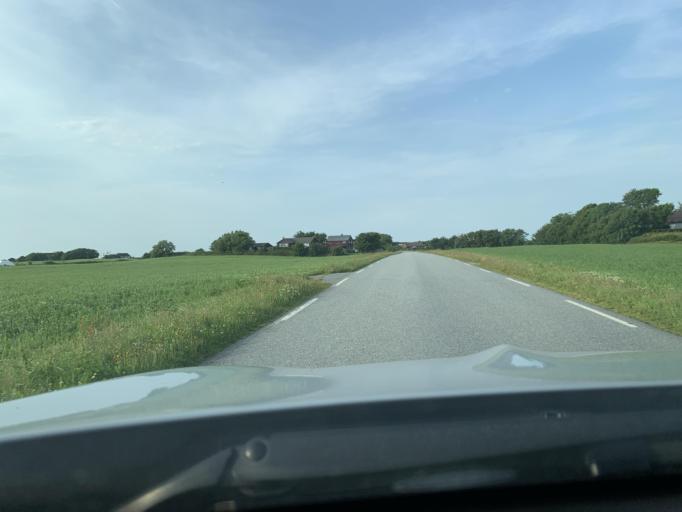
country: NO
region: Rogaland
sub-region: Time
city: Bryne
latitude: 58.7257
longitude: 5.5837
